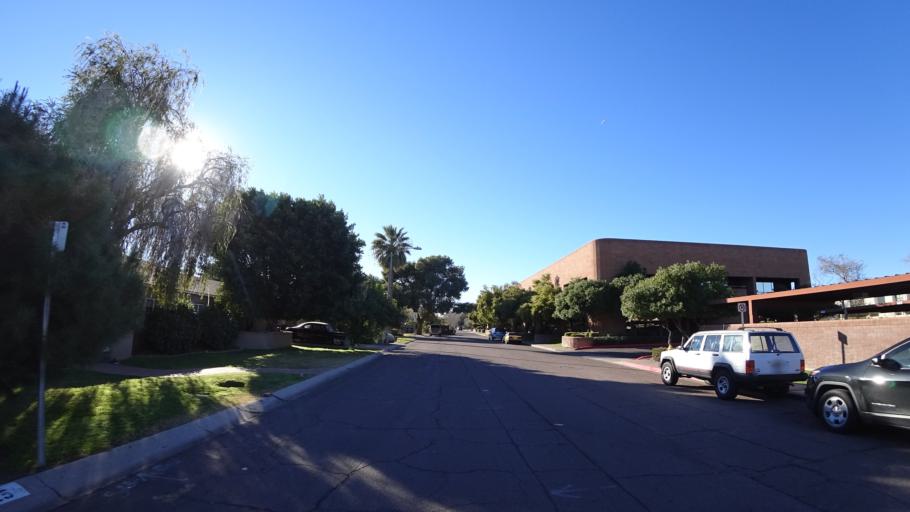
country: US
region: Arizona
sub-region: Maricopa County
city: Phoenix
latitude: 33.5138
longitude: -112.0722
